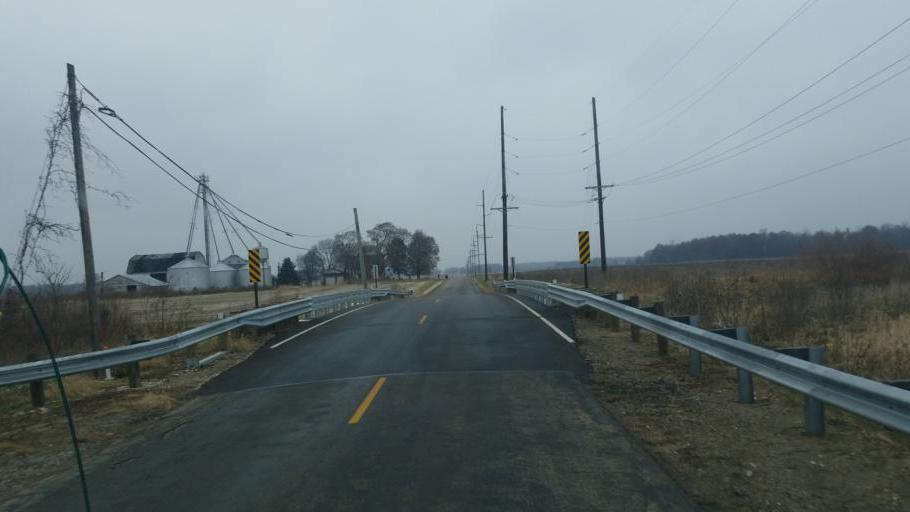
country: US
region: Ohio
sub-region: Richland County
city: Shelby
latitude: 40.9165
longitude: -82.6859
